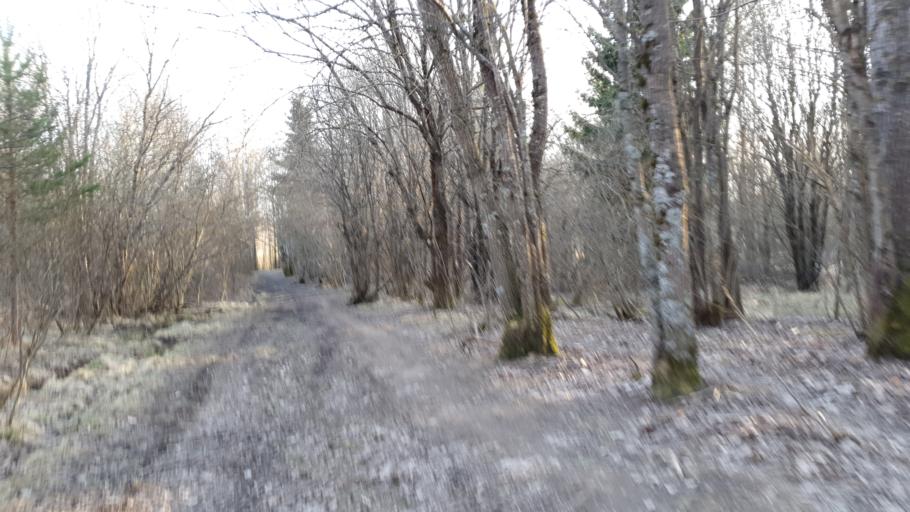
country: FI
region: Uusimaa
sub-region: Helsinki
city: Nurmijaervi
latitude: 60.3360
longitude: 24.8438
